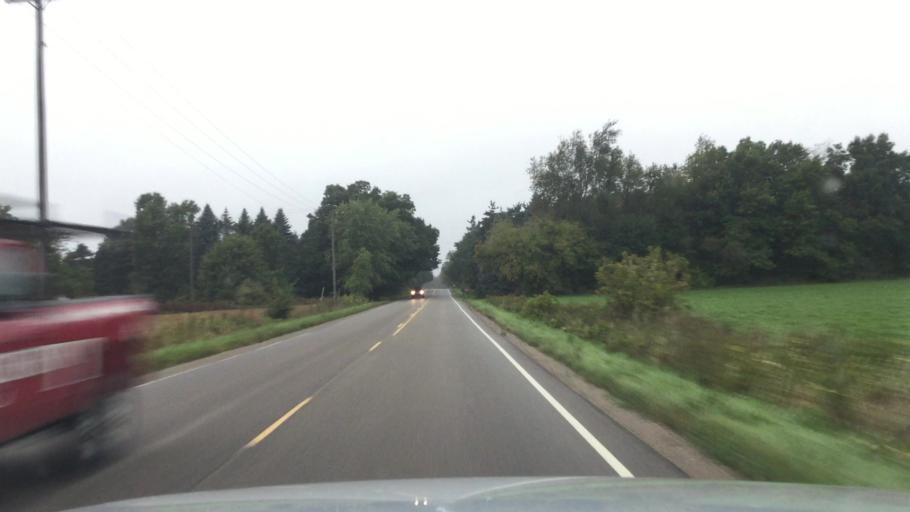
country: US
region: Michigan
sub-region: Shiawassee County
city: Corunna
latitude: 42.8991
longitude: -84.1124
